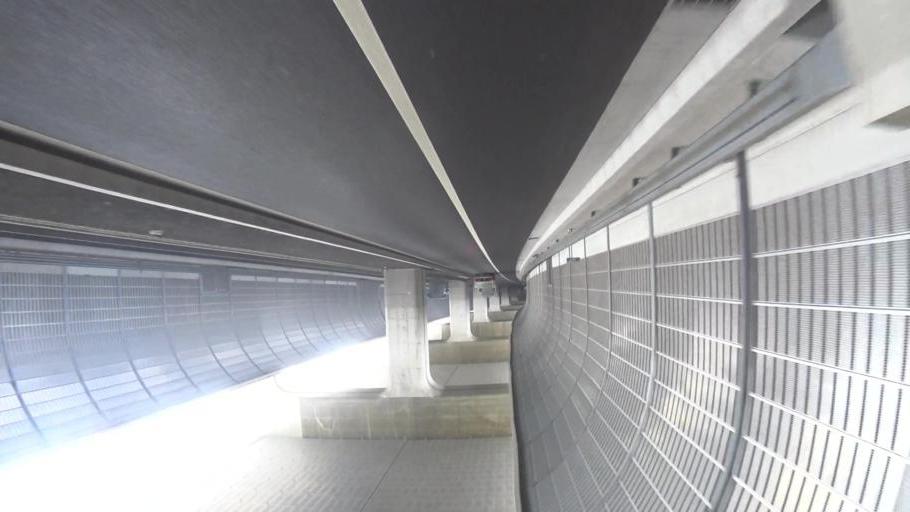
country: JP
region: Osaka
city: Hirakata
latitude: 34.7963
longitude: 135.7010
